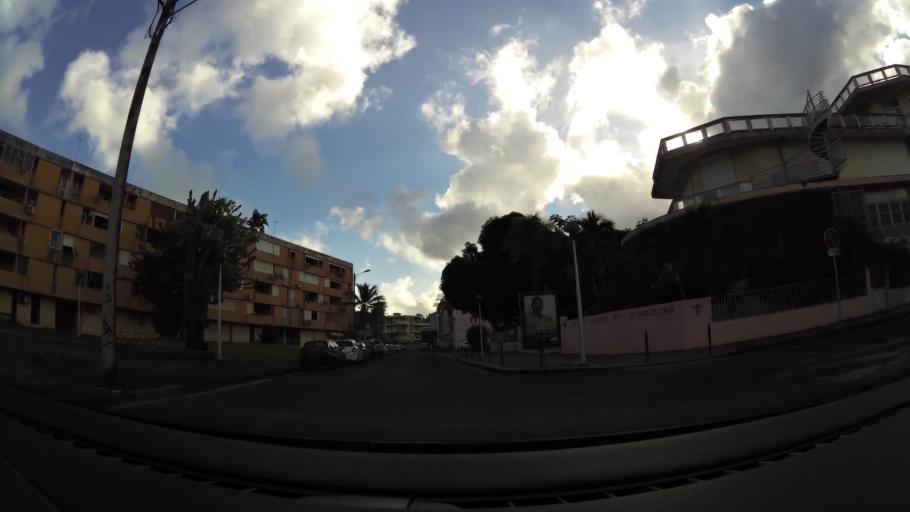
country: GP
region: Guadeloupe
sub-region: Guadeloupe
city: Pointe-a-Pitre
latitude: 16.2452
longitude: -61.5334
